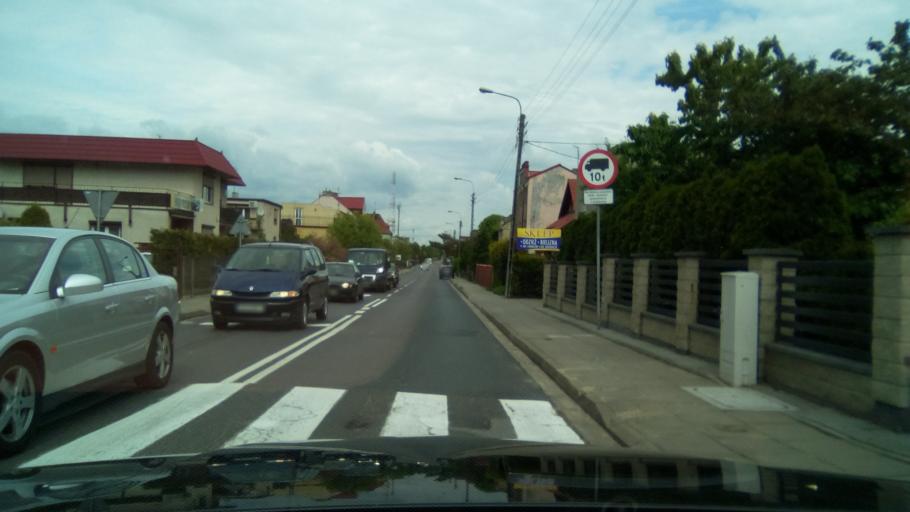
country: PL
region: Greater Poland Voivodeship
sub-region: Powiat gnieznienski
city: Gniezno
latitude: 52.5204
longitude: 17.6057
